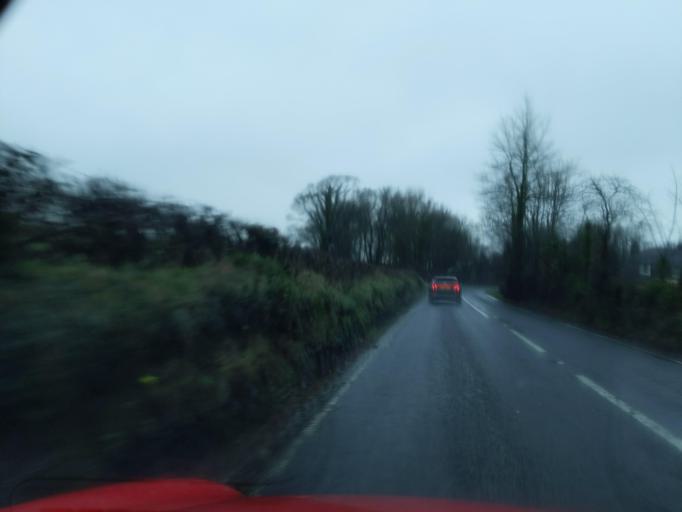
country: GB
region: England
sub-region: Cornwall
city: South Hill
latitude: 50.5512
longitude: -4.3327
